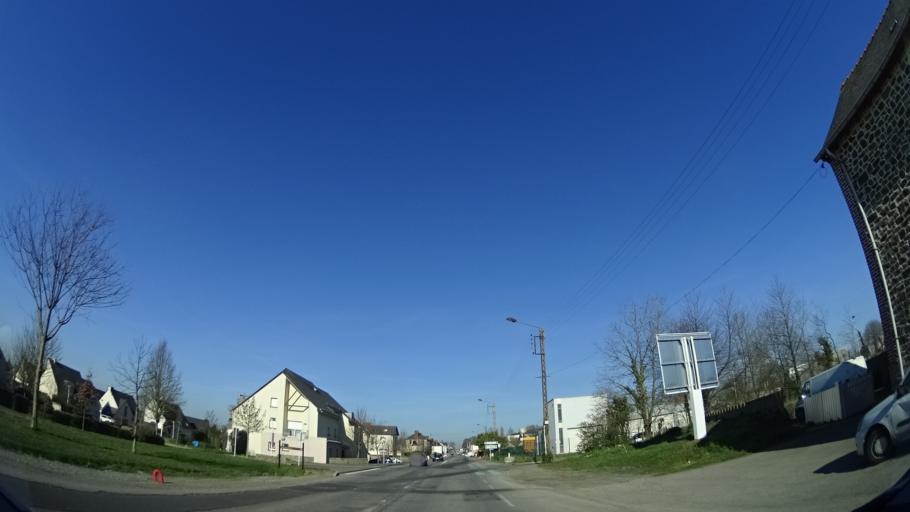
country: FR
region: Brittany
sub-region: Departement d'Ille-et-Vilaine
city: La Meziere
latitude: 48.2156
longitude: -1.7459
